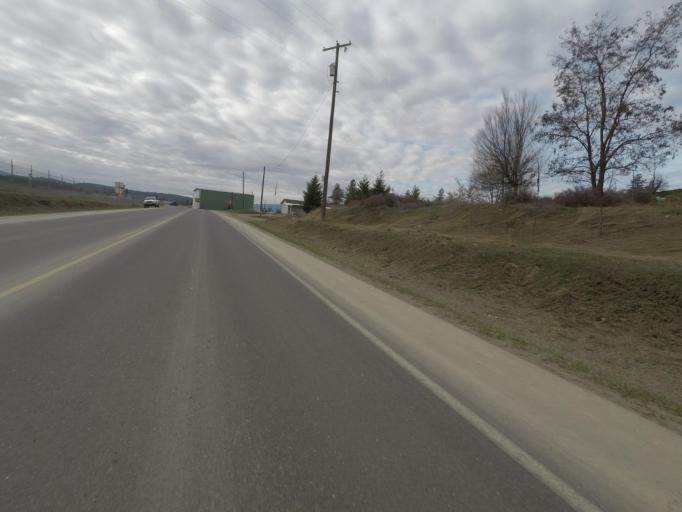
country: US
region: Washington
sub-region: Stevens County
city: Colville
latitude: 48.5482
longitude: -117.8821
